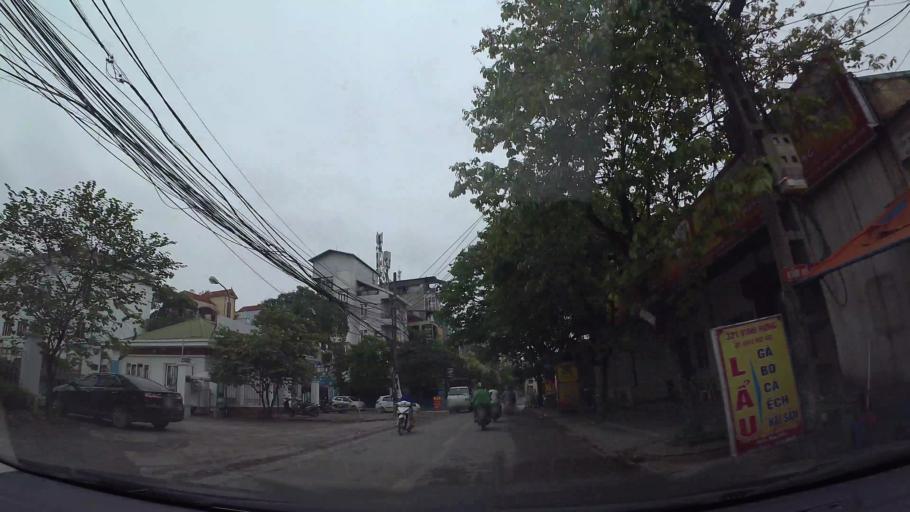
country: VN
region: Ha Noi
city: Hai BaTrung
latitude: 20.9961
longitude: 105.8799
